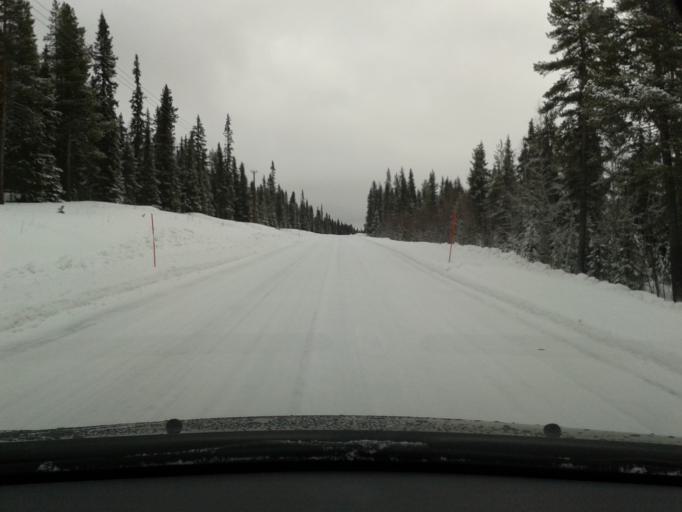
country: SE
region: Vaesterbotten
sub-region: Vilhelmina Kommun
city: Sjoberg
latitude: 65.2374
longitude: 15.8193
